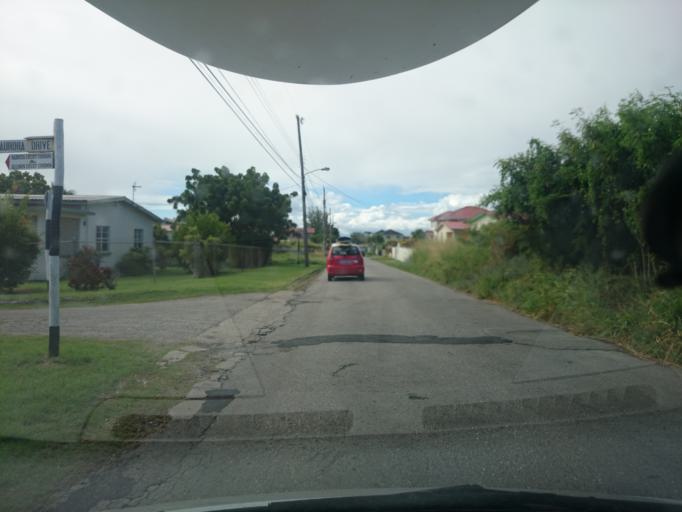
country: BB
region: Christ Church
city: Oistins
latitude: 13.0524
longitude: -59.5323
